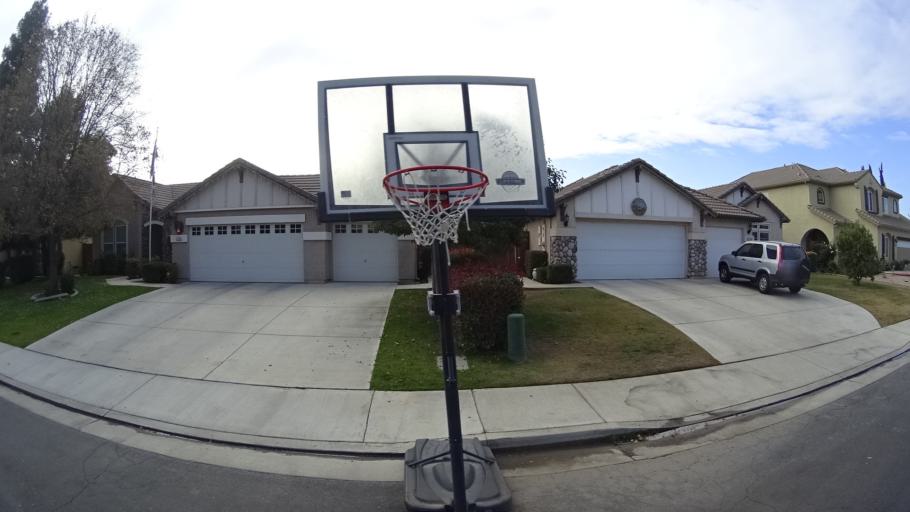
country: US
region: California
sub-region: Kern County
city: Greenacres
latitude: 35.3012
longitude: -119.1262
